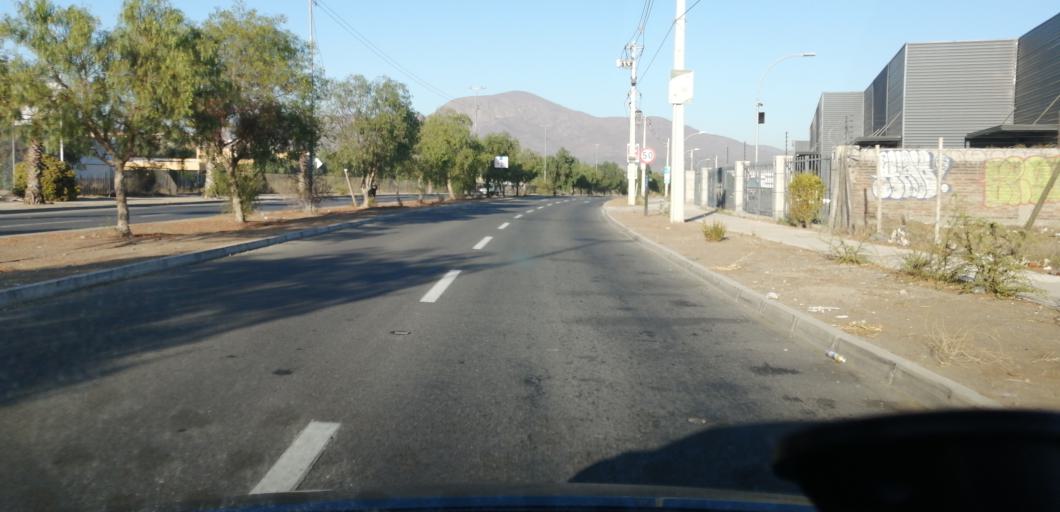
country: CL
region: Santiago Metropolitan
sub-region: Provincia de Santiago
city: Lo Prado
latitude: -33.4485
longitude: -70.8463
